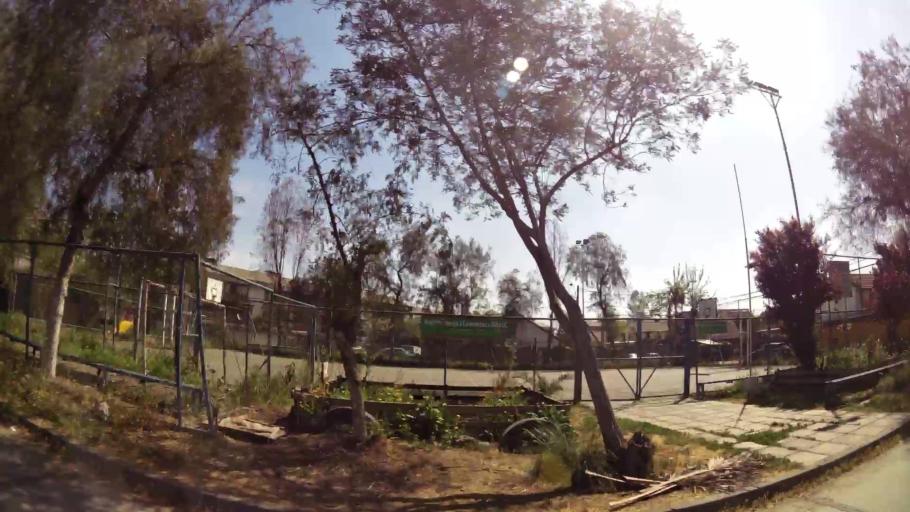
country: CL
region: Santiago Metropolitan
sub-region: Provincia de Santiago
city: Villa Presidente Frei, Nunoa, Santiago, Chile
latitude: -33.4800
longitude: -70.5814
